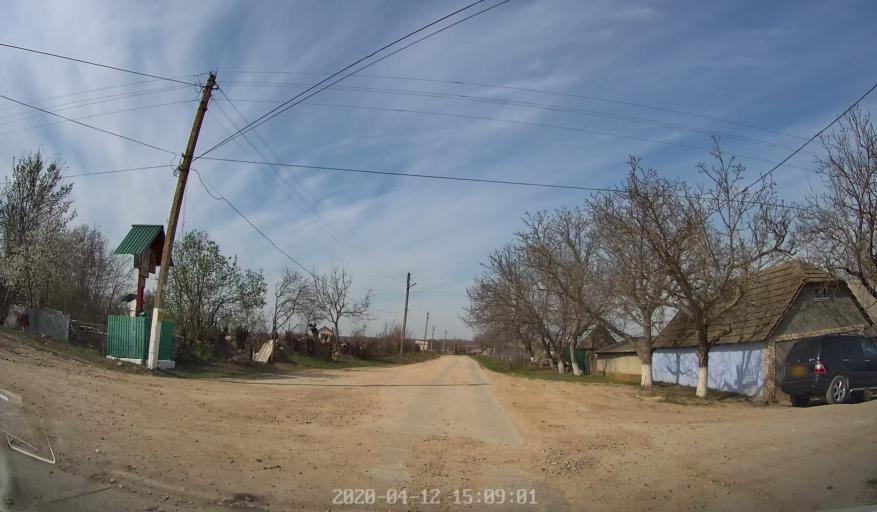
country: MD
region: Telenesti
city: Cocieri
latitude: 47.3186
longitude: 29.0694
